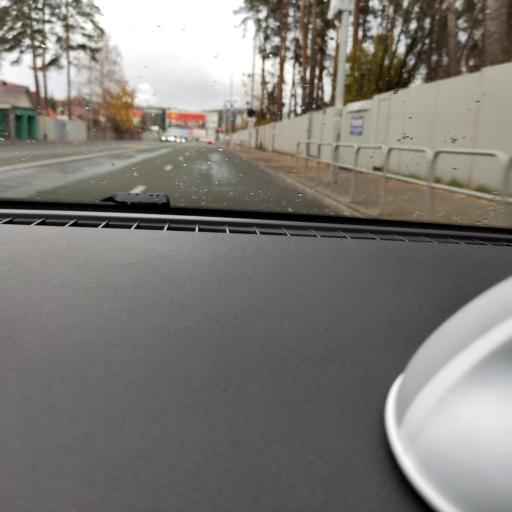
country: RU
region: Samara
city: Samara
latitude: 53.2657
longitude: 50.2424
